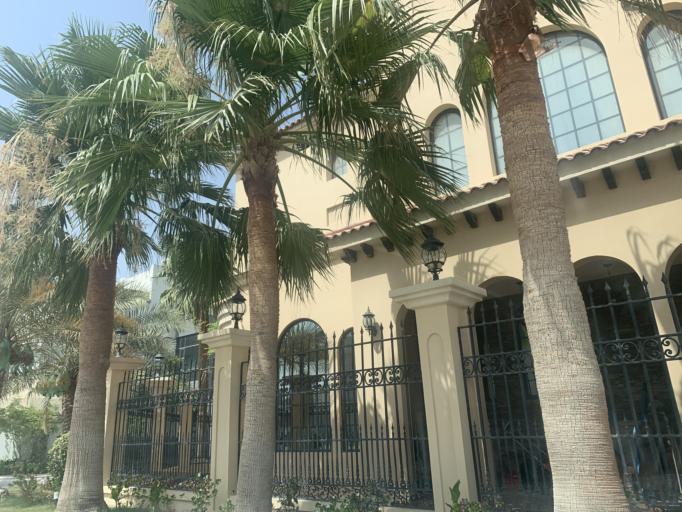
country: BH
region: Northern
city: Madinat `Isa
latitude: 26.1946
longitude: 50.4903
